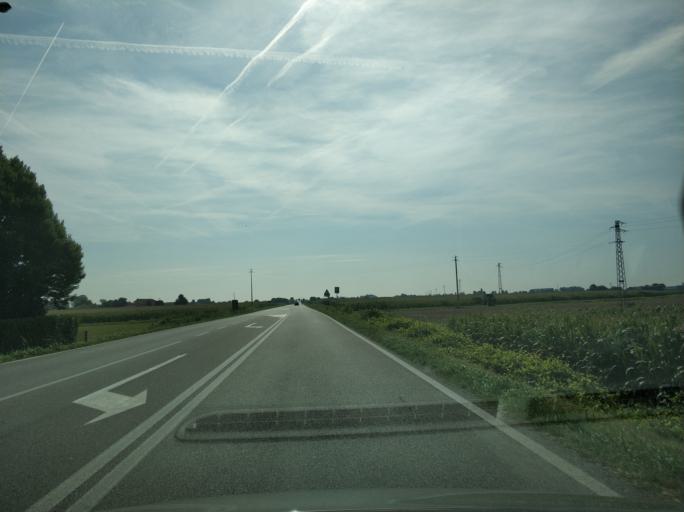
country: IT
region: Veneto
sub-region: Provincia di Padova
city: Conselve
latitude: 45.2142
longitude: 11.8676
